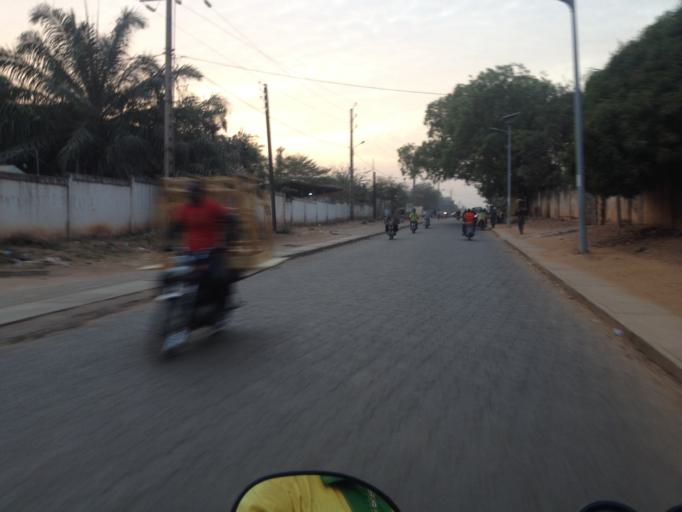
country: BJ
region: Borgou
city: Parakou
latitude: 9.3367
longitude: 2.6380
